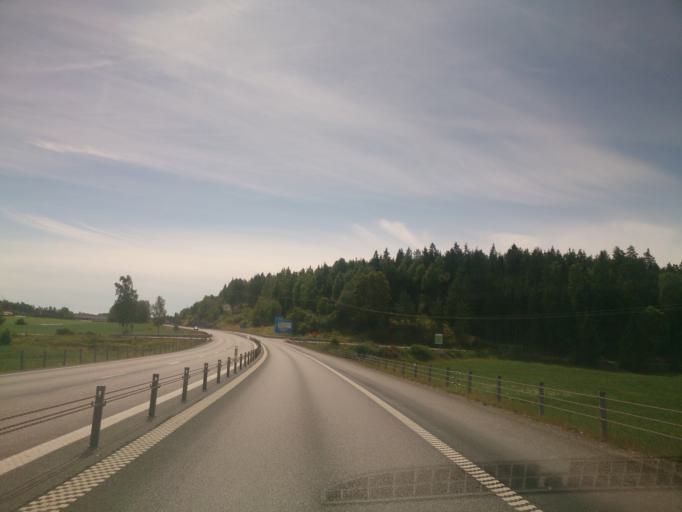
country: SE
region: OEstergoetland
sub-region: Valdemarsviks Kommun
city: Gusum
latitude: 58.2900
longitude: 16.4967
